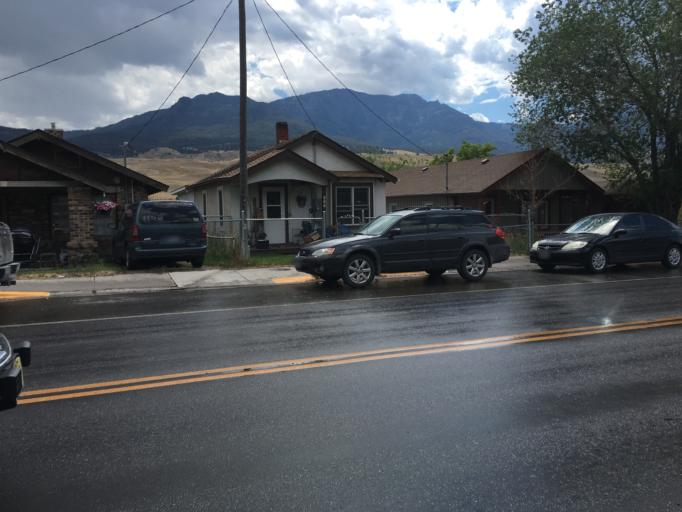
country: US
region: Montana
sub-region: Gallatin County
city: West Yellowstone
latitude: 45.0341
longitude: -110.7080
